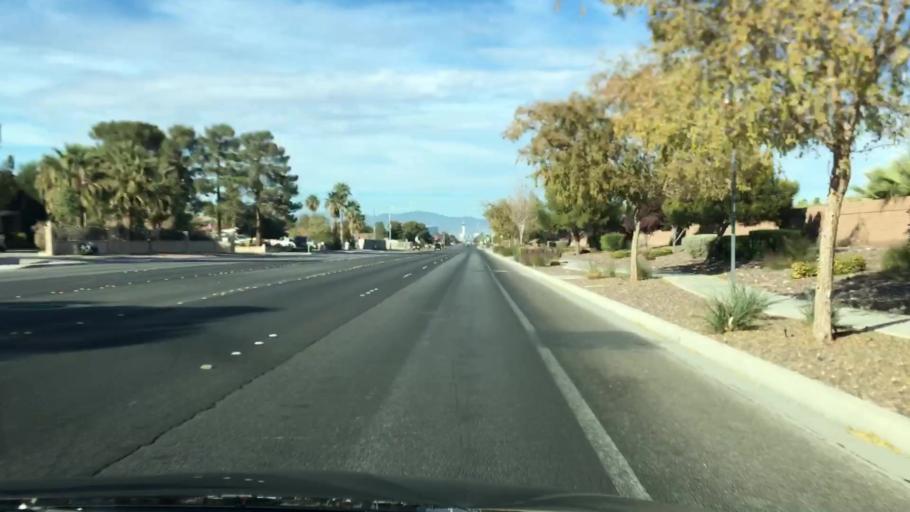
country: US
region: Nevada
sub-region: Clark County
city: Paradise
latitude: 36.0475
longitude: -115.1543
